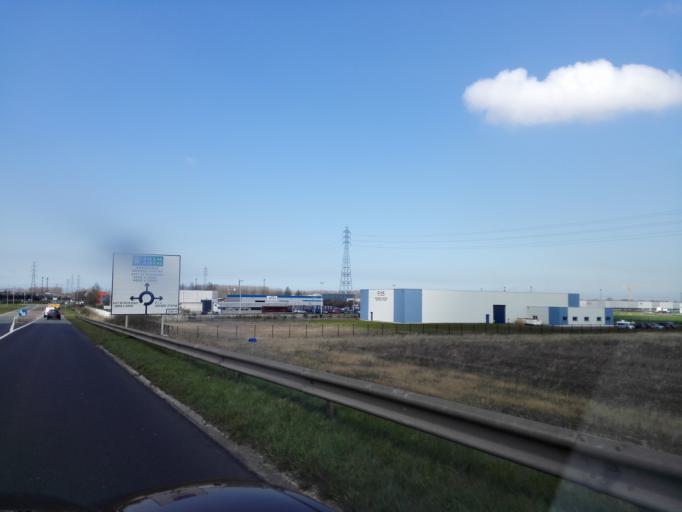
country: FR
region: Nord-Pas-de-Calais
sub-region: Departement du Nord
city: Grande-Synthe
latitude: 50.9899
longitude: 2.2991
